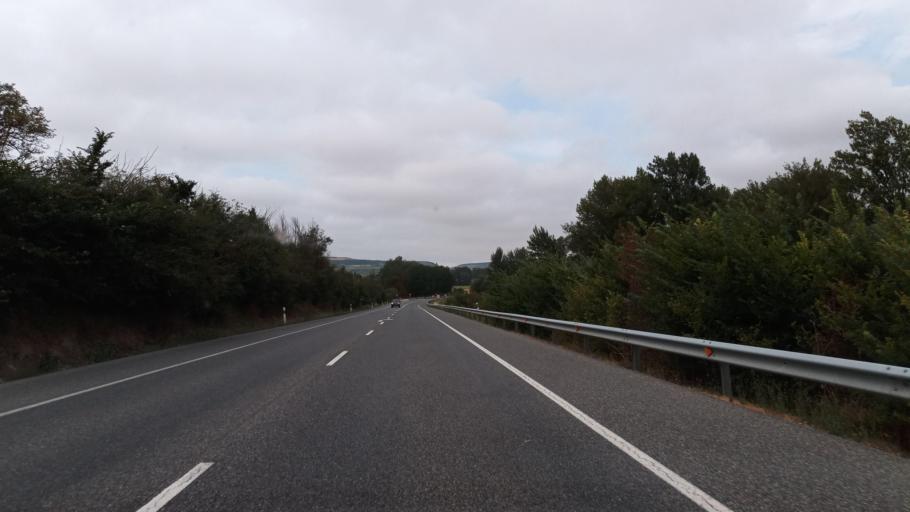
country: ES
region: Castille and Leon
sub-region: Provincia de Burgos
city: Santa Olalla de Bureba
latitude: 42.4672
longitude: -3.4348
